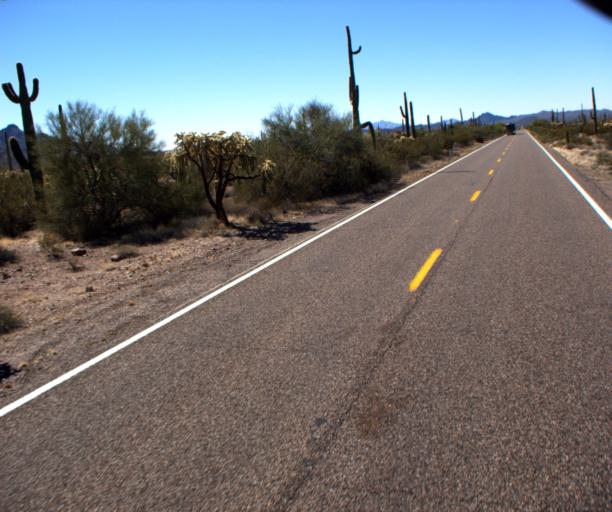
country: MX
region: Sonora
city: Sonoyta
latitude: 32.0765
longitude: -112.7808
